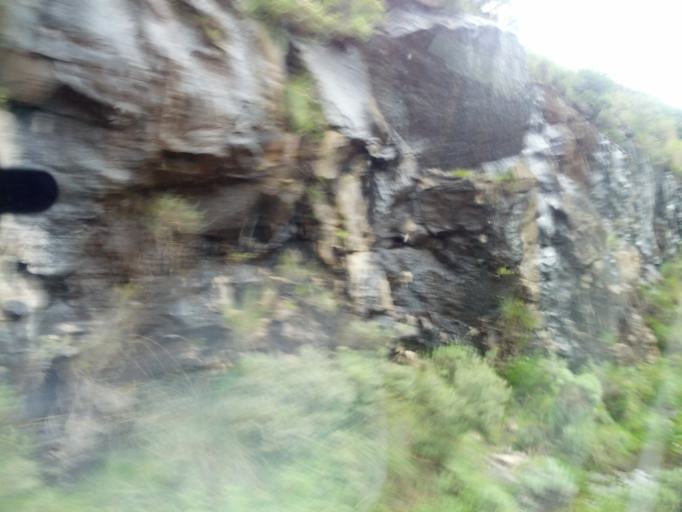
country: LS
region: Butha-Buthe
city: Butha-Buthe
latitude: -29.0624
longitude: 28.3635
